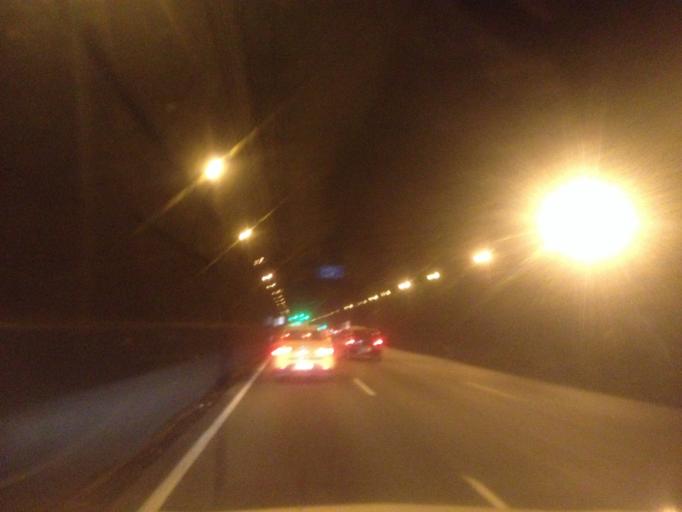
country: BR
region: Rio de Janeiro
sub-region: Rio De Janeiro
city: Rio de Janeiro
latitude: -22.9572
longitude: -43.2043
